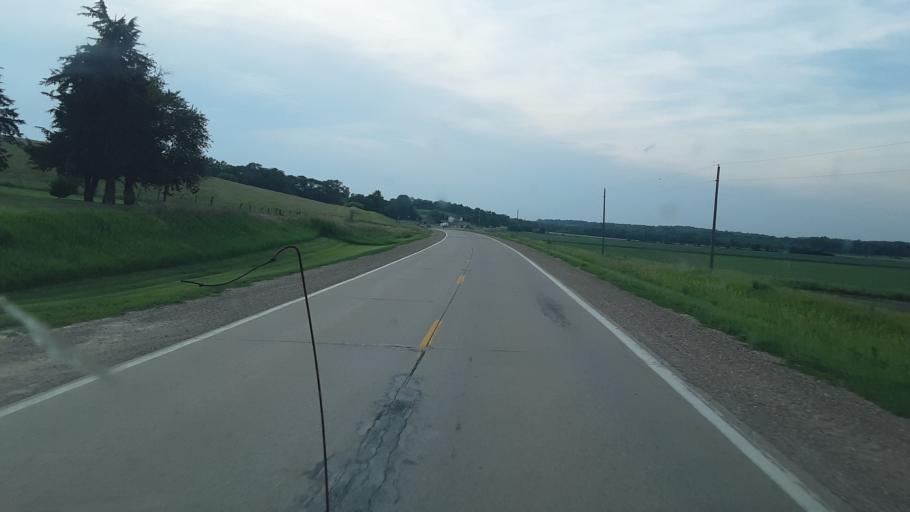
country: US
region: Iowa
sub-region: Tama County
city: Toledo
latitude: 41.9958
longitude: -92.7266
